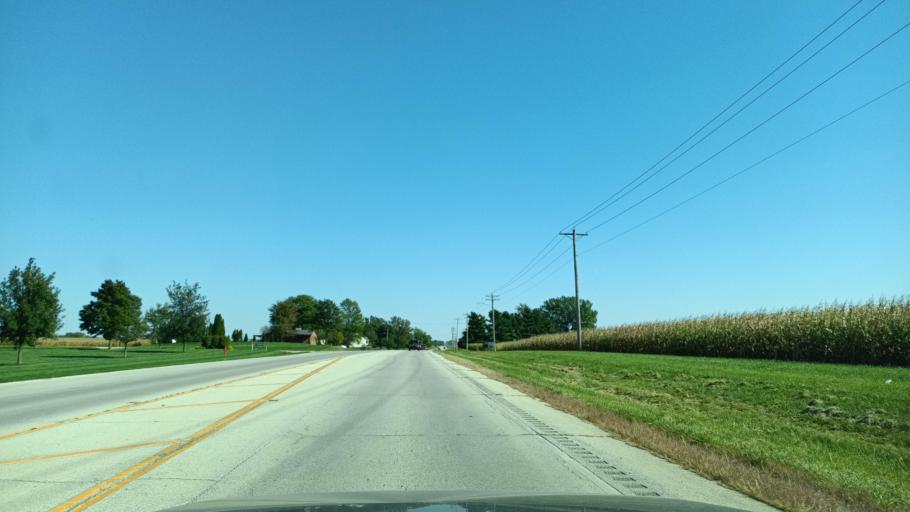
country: US
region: Illinois
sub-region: Champaign County
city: Lake of the Woods
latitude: 40.1830
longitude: -88.3620
